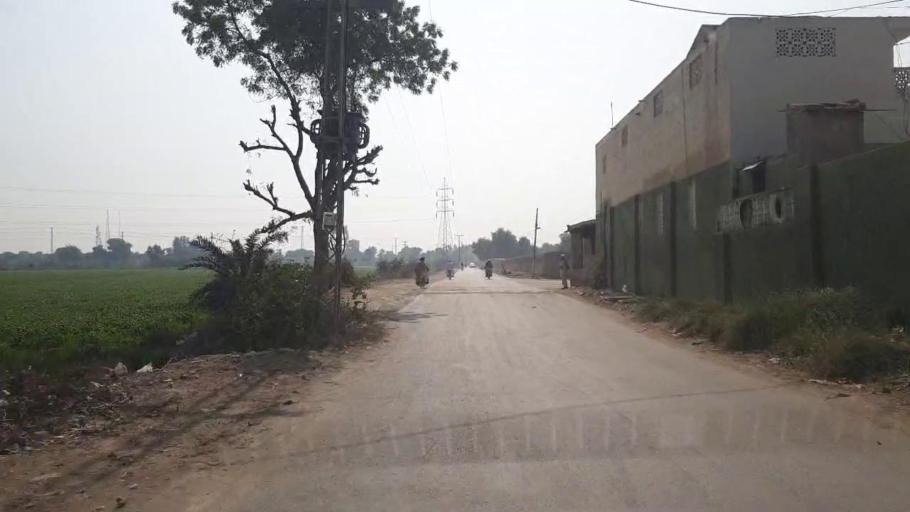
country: PK
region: Sindh
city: Hala
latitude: 25.8236
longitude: 68.4192
